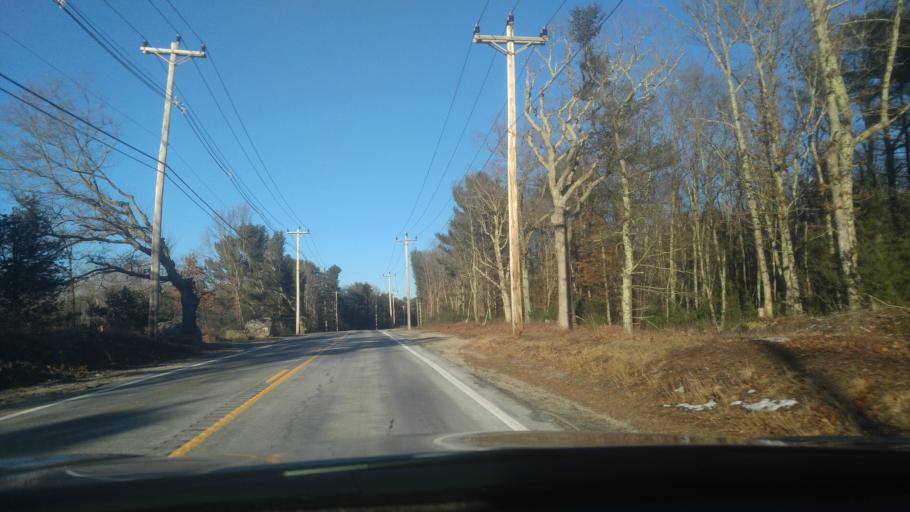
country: US
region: Rhode Island
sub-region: Kent County
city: West Warwick
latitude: 41.6533
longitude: -71.5634
